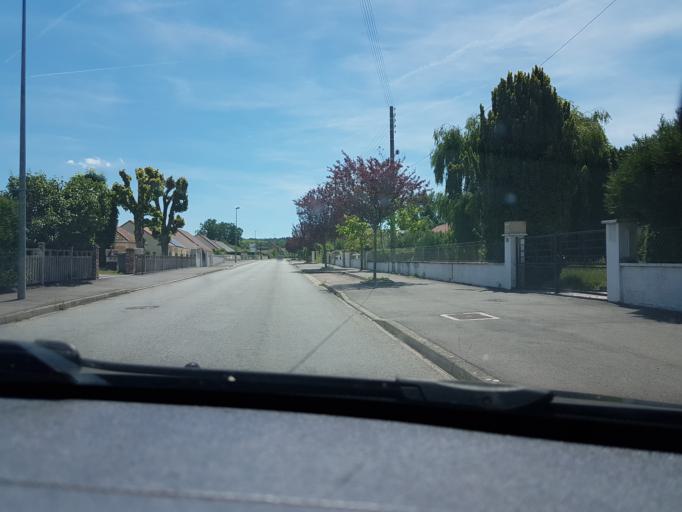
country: FR
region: Bourgogne
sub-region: Departement de Saone-et-Loire
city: Epinac
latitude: 46.9866
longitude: 4.5096
